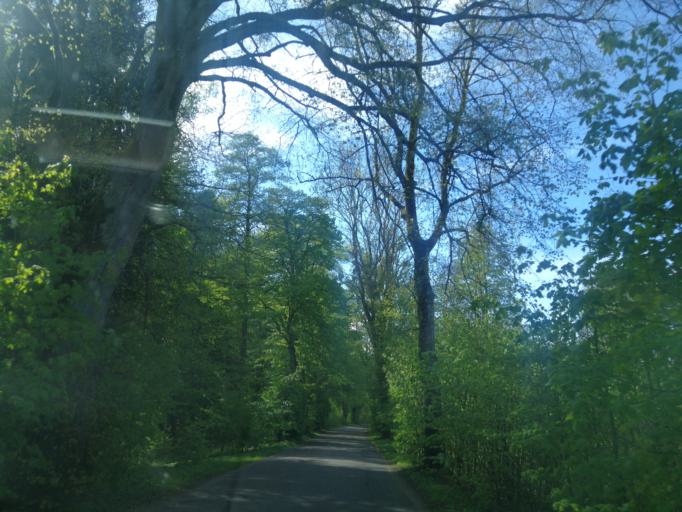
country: PL
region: Warmian-Masurian Voivodeship
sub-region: Powiat ilawski
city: Zalewo
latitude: 53.7077
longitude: 19.6861
